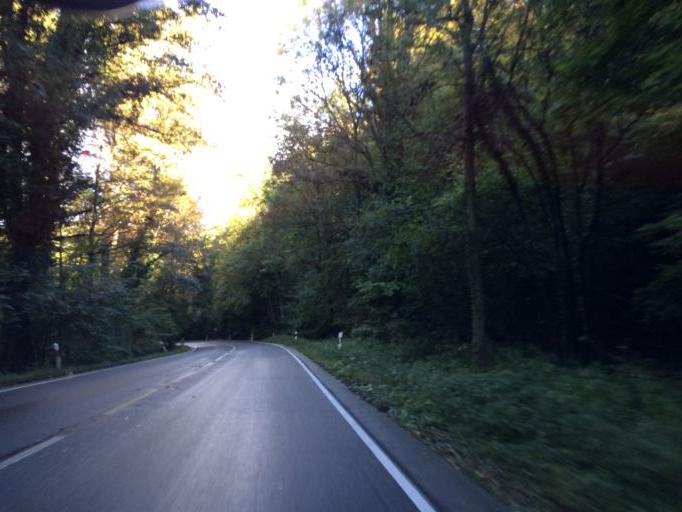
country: DE
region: North Rhine-Westphalia
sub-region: Regierungsbezirk Koln
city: Bad Honnef
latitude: 50.6792
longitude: 7.2238
